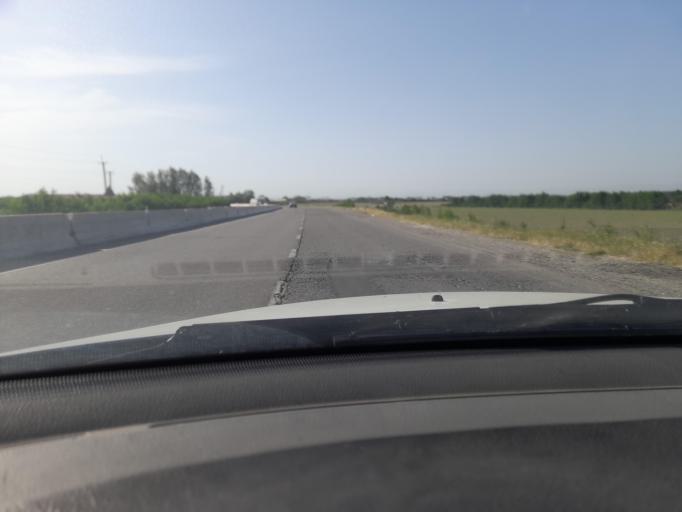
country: UZ
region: Samarqand
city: Kattaqo'rg'on
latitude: 39.9259
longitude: 66.2740
